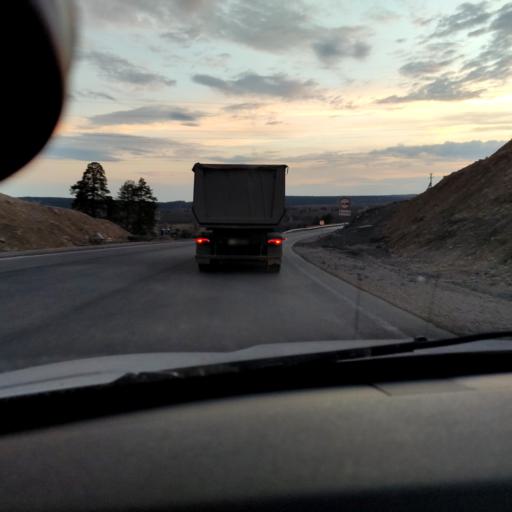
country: RU
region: Perm
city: Chusovoy
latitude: 58.3300
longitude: 57.7897
